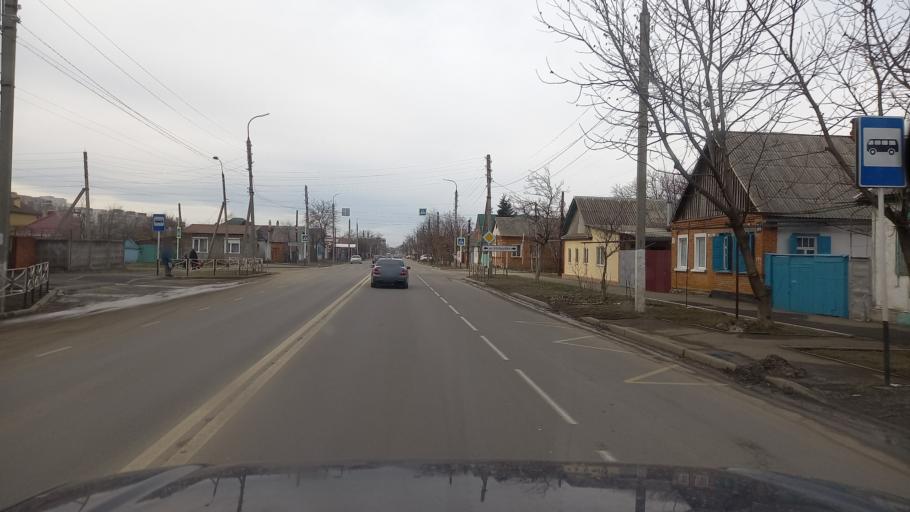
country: RU
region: Adygeya
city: Maykop
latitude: 44.6145
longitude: 40.0881
